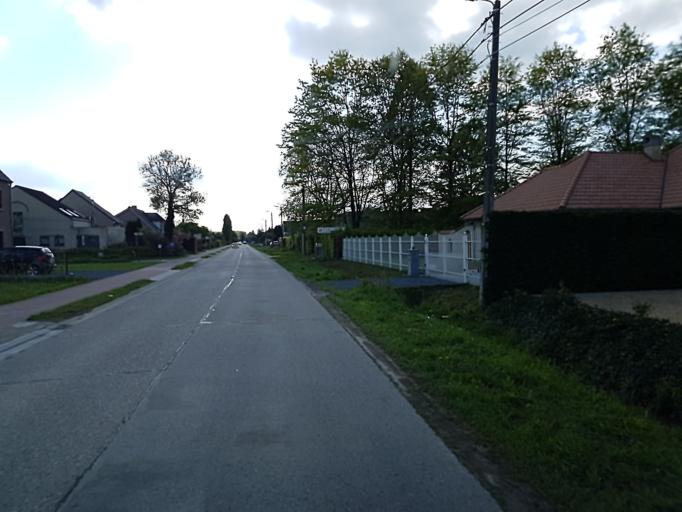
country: BE
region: Flanders
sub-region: Provincie Vlaams-Brabant
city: Tremelo
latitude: 51.0221
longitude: 4.7186
